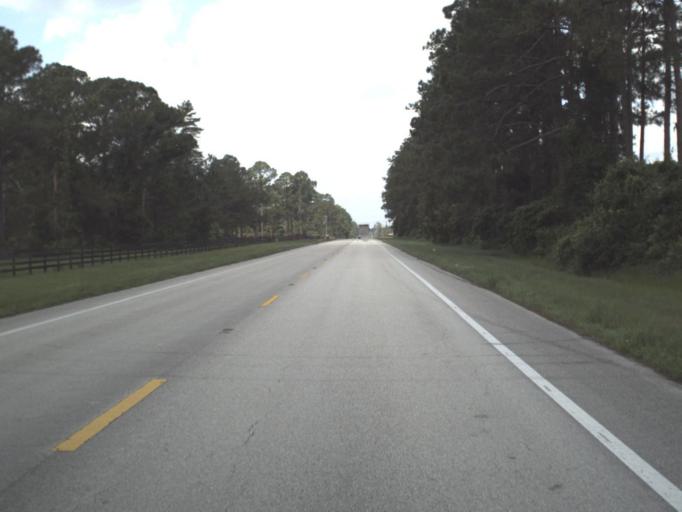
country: US
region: Florida
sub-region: Saint Johns County
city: Saint Augustine Shores
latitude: 29.7259
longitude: -81.4369
